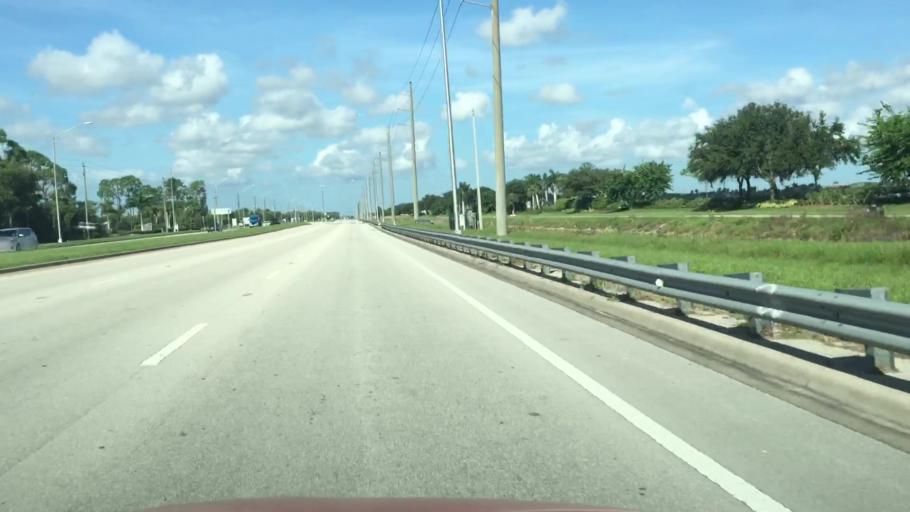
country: US
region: Florida
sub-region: Collier County
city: Vineyards
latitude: 26.2732
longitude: -81.6663
